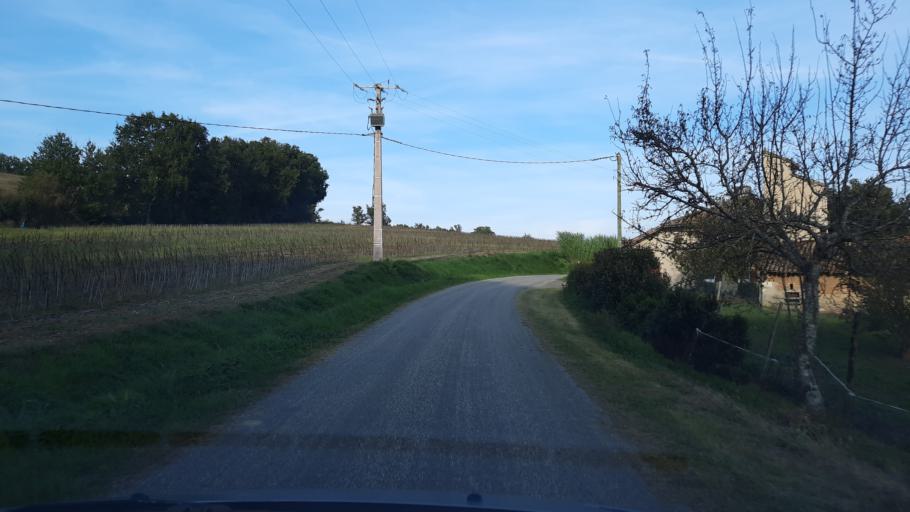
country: FR
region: Midi-Pyrenees
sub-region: Departement du Tarn-et-Garonne
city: Lafrancaise
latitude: 44.1719
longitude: 1.2913
